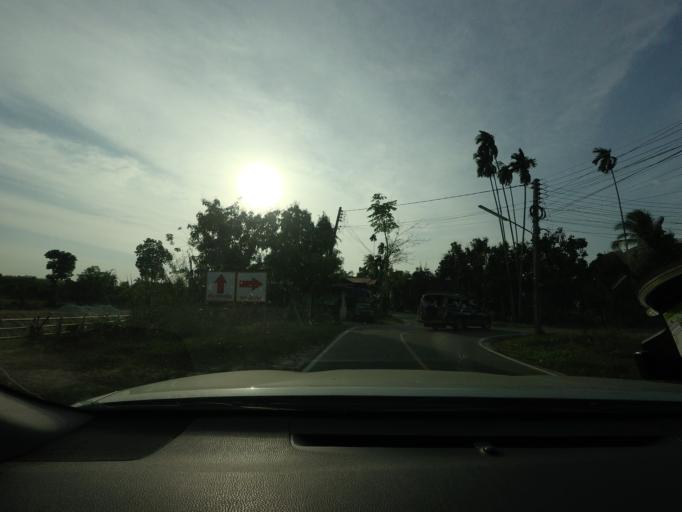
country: TH
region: Narathiwat
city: Ra-ngae
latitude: 6.2965
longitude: 101.7338
